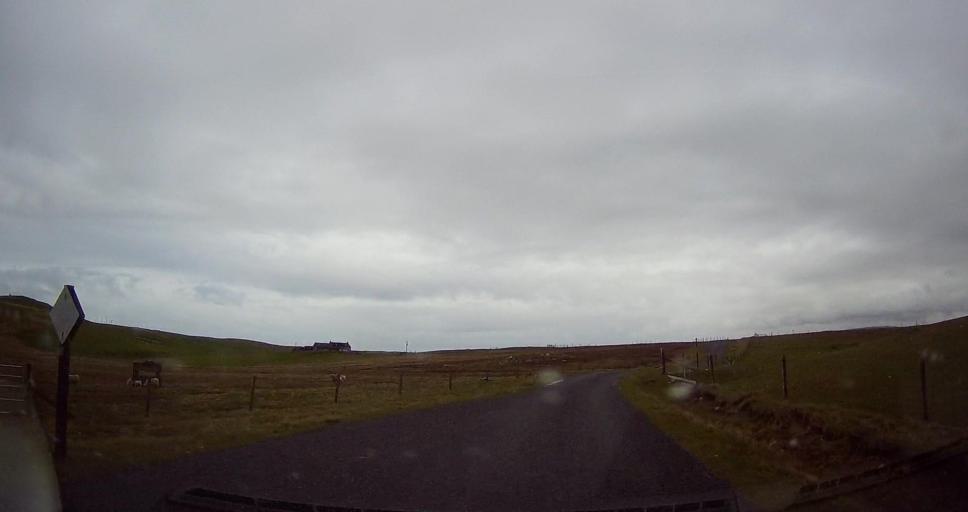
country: GB
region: Scotland
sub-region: Shetland Islands
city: Lerwick
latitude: 60.4793
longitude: -1.6128
